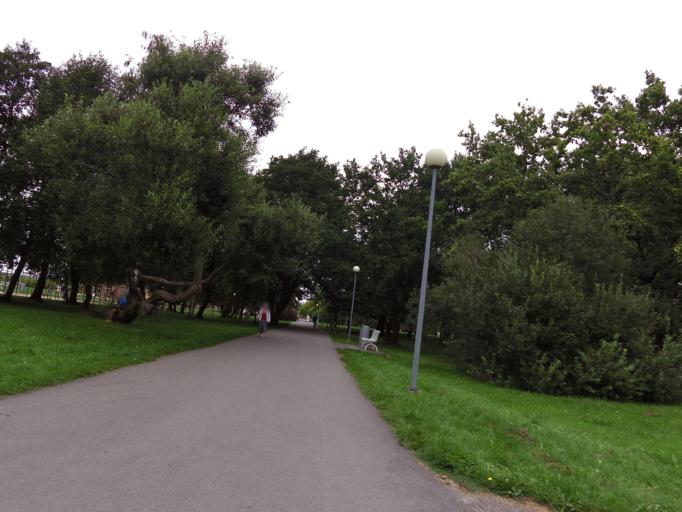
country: EE
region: Harju
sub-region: Tallinna linn
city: Tallinn
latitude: 59.4394
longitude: 24.6838
